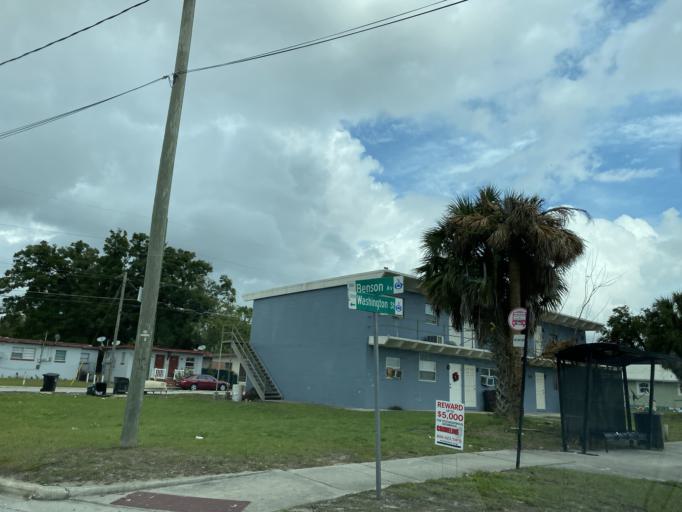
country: US
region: Florida
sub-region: Orange County
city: Orlando
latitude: 28.5439
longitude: -81.3952
